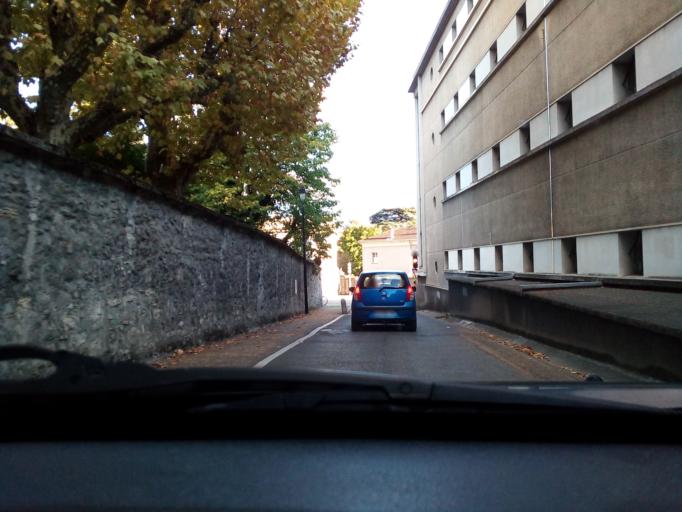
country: FR
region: Rhone-Alpes
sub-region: Departement de l'Isere
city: La Tronche
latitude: 45.2058
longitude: 5.7480
